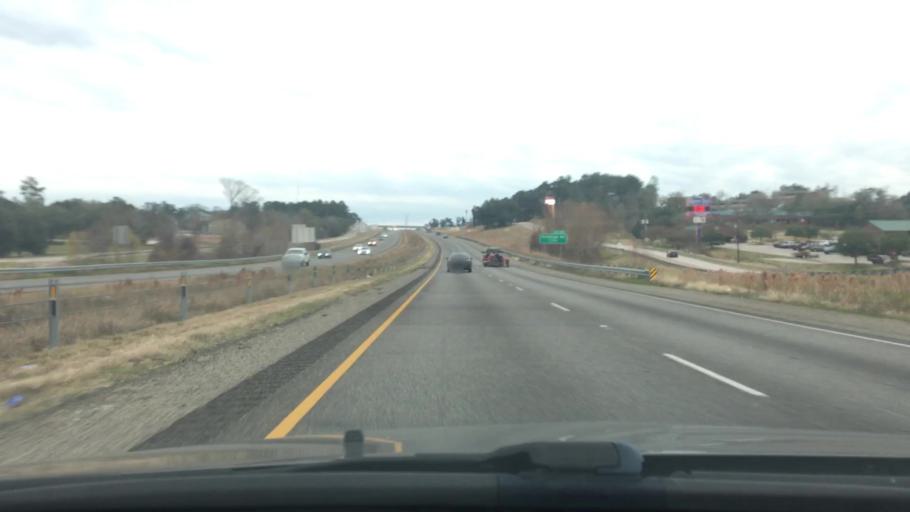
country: US
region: Texas
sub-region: Walker County
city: Huntsville
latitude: 30.7039
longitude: -95.5603
